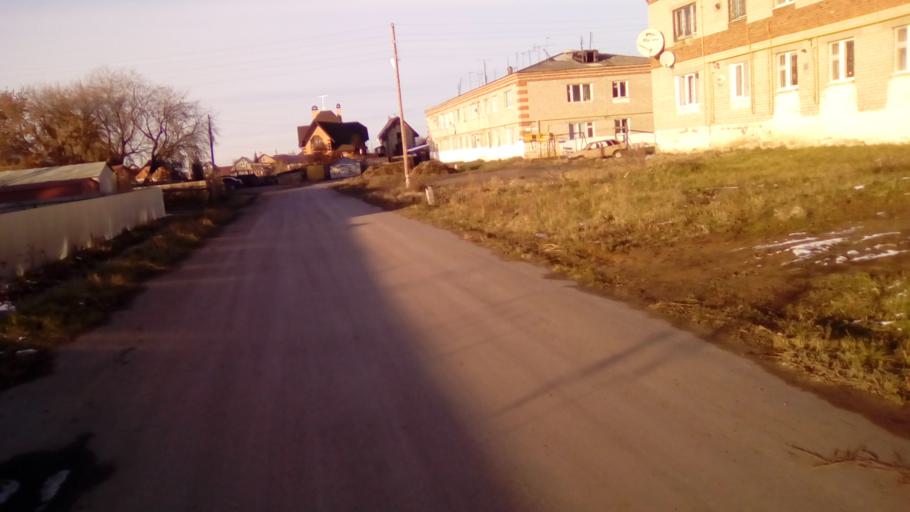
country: RU
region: Tjumen
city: Moskovskiy
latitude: 57.2207
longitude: 65.3552
